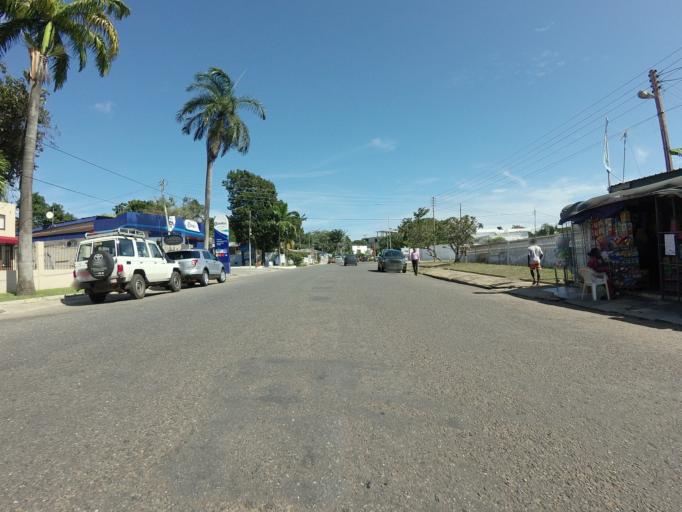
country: GH
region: Greater Accra
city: Accra
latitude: 5.5715
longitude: -0.1693
